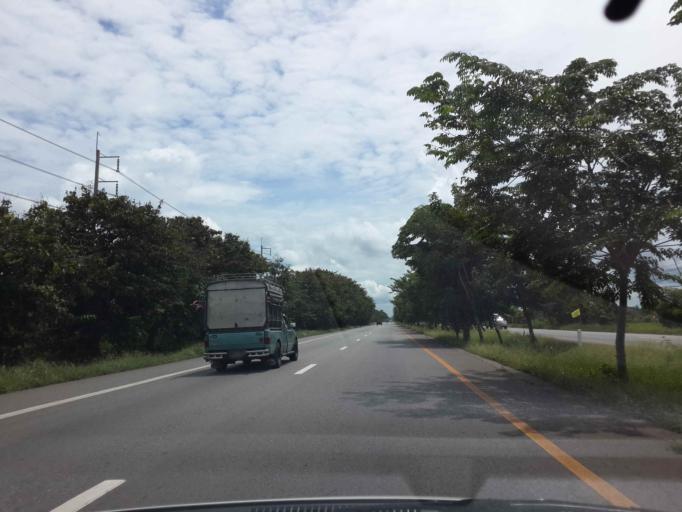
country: TH
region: Ratchaburi
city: Pak Tho
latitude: 13.3873
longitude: 99.8181
